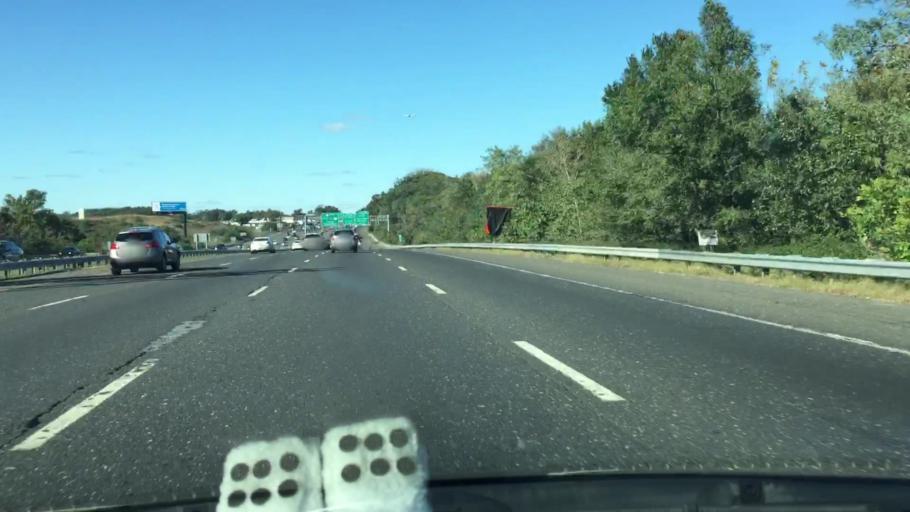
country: US
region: New Jersey
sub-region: Camden County
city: Bellmawr
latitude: 39.8557
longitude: -75.0980
